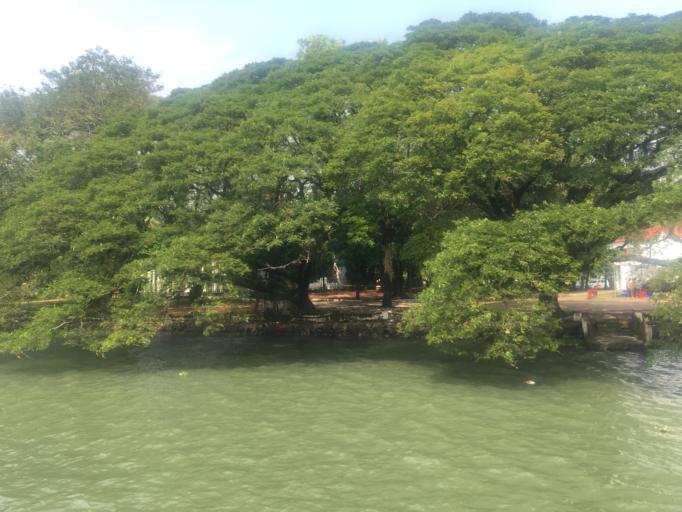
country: IN
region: Kerala
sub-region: Ernakulam
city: Cochin
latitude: 9.9829
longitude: 76.2672
